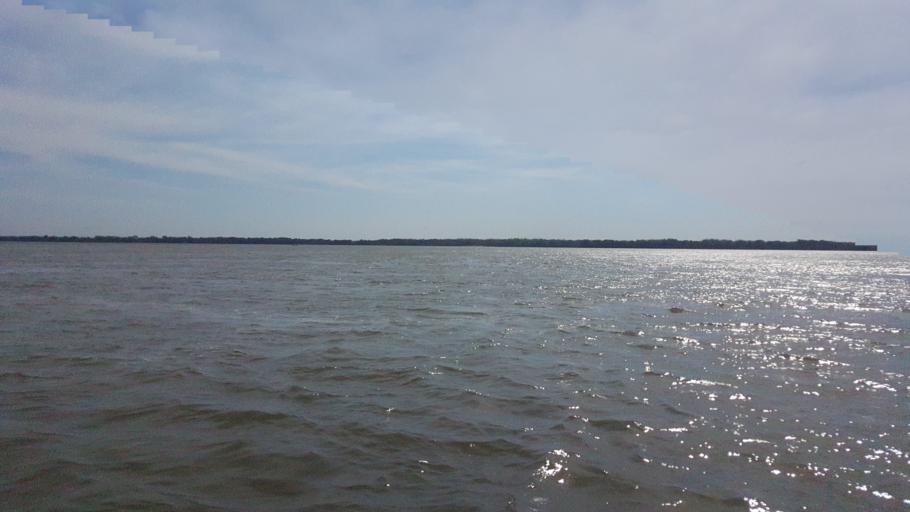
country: AR
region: Corrientes
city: Ituzaingo
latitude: -27.6073
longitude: -56.8410
